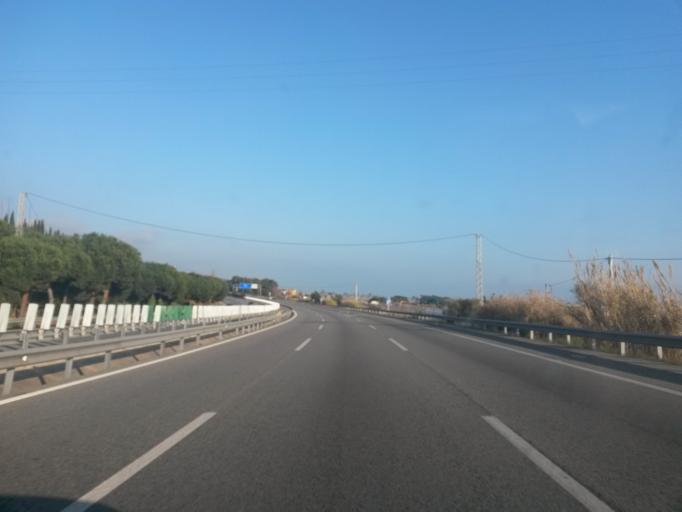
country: ES
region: Catalonia
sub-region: Provincia de Barcelona
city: Sant Andreu de Llavaneres
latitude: 41.5583
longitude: 2.4813
